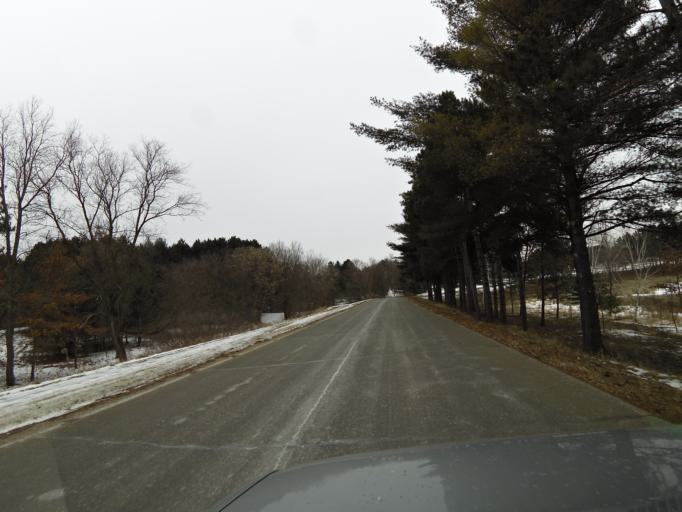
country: US
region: Minnesota
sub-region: Washington County
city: Lake Elmo
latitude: 44.9732
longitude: -92.9039
